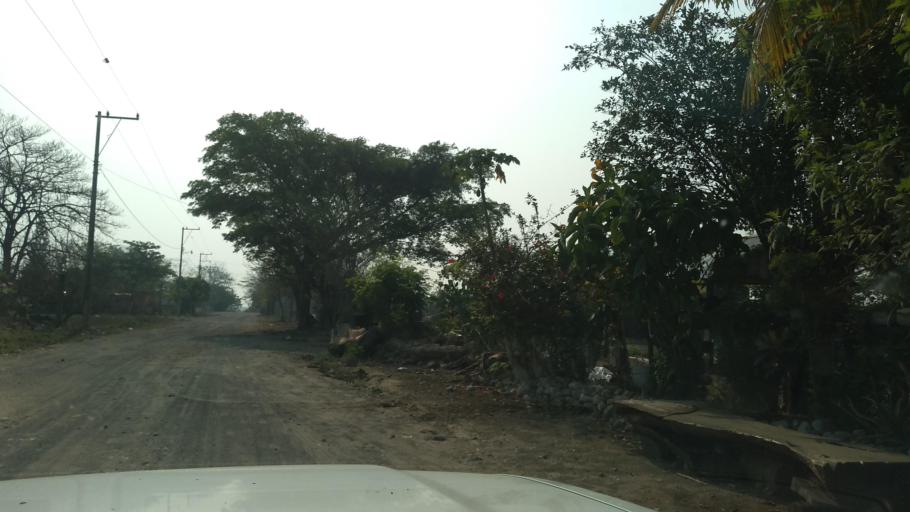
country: MX
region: Oaxaca
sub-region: Cosolapa
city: Cosolapa
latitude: 18.6225
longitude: -96.6029
